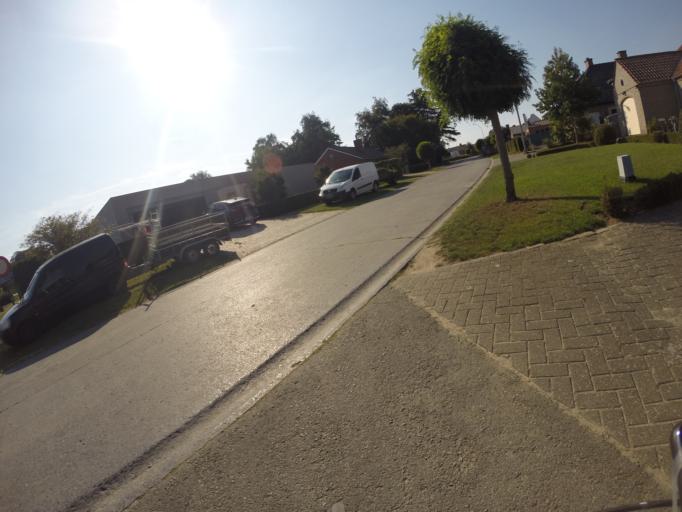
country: BE
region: Flanders
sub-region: Provincie Oost-Vlaanderen
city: Aalter
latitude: 51.0884
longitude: 3.4592
